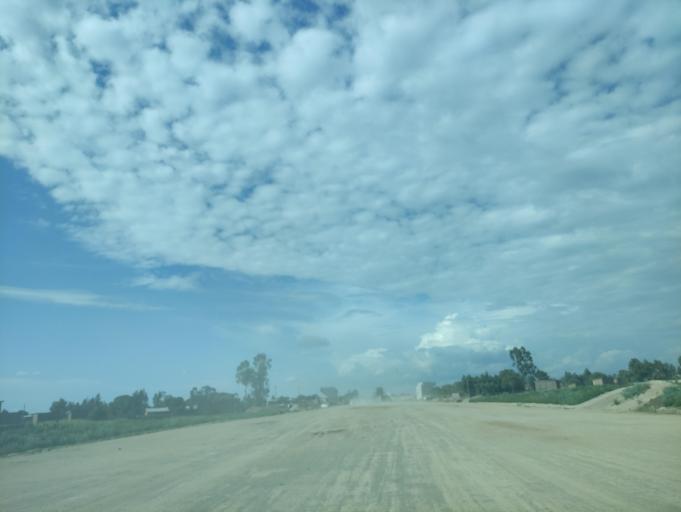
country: ET
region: Oromiya
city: Shashemene
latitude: 7.2213
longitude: 38.5580
